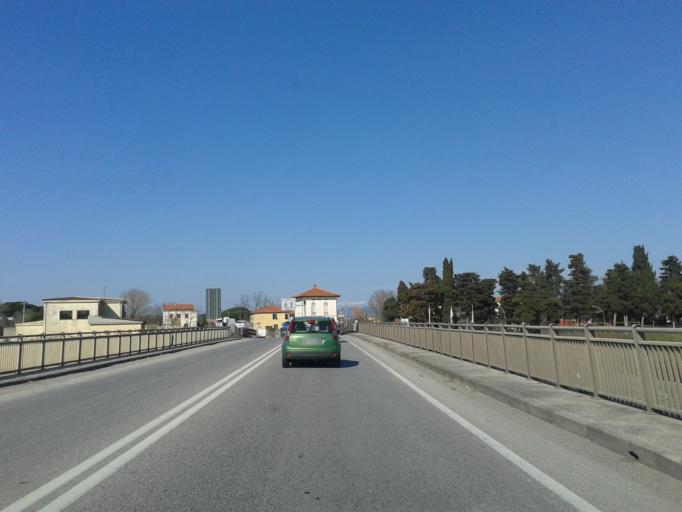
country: IT
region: Tuscany
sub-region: Provincia di Livorno
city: Guasticce
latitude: 43.6001
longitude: 10.3523
